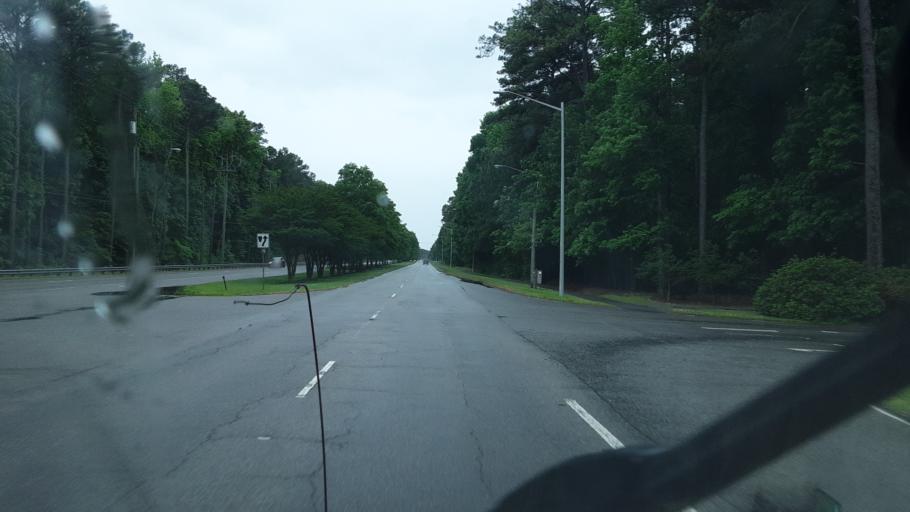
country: US
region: Virginia
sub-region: City of Virginia Beach
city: Virginia Beach
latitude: 36.8056
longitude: -75.9917
